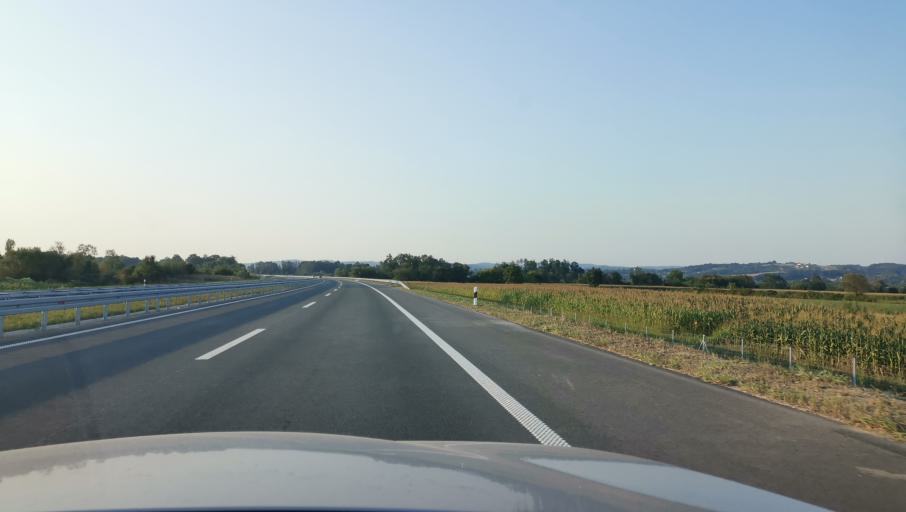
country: RS
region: Central Serbia
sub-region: Kolubarski Okrug
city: Ljig
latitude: 44.2608
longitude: 20.2711
